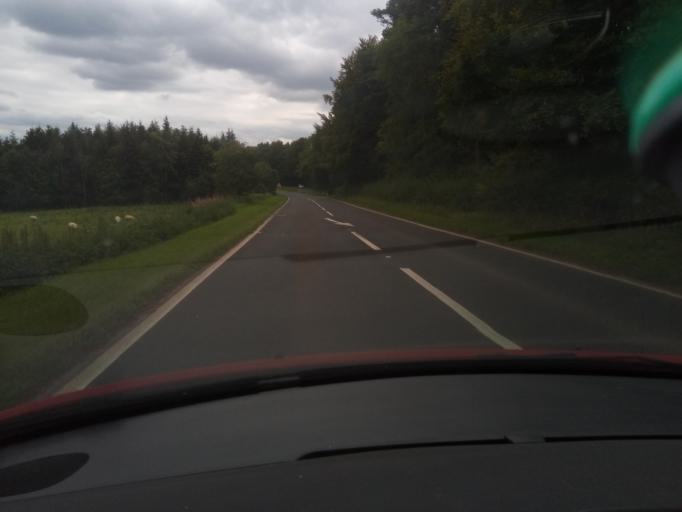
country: GB
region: Scotland
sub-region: The Scottish Borders
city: Jedburgh
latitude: 55.3941
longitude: -2.4989
